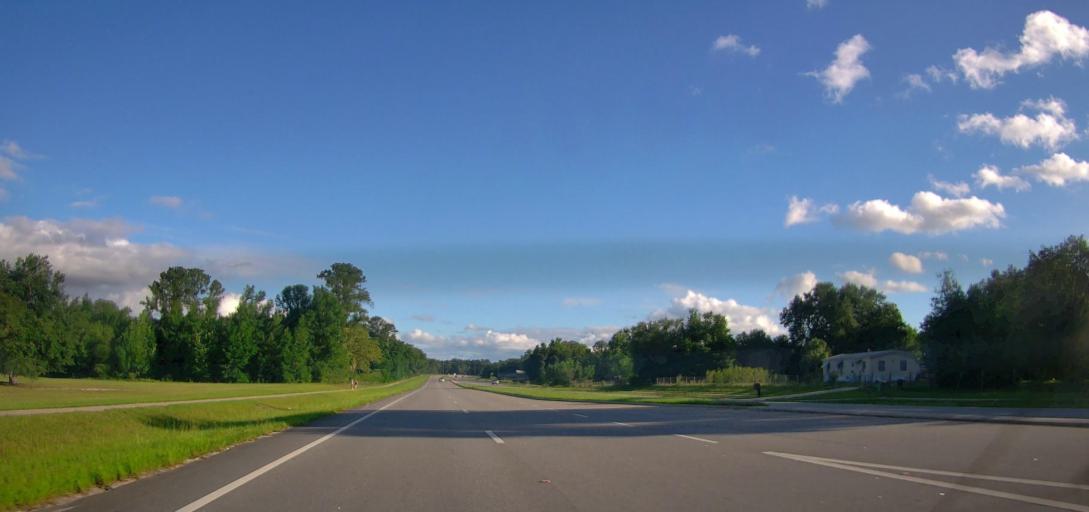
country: US
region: Florida
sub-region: Marion County
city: Belleview
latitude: 29.0414
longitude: -82.0175
